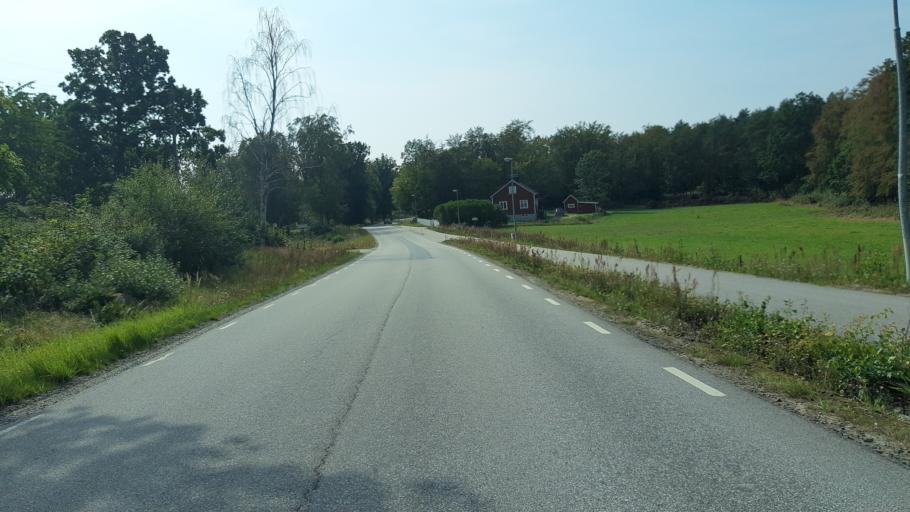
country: SE
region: Blekinge
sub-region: Ronneby Kommun
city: Ronneby
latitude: 56.1720
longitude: 15.2405
